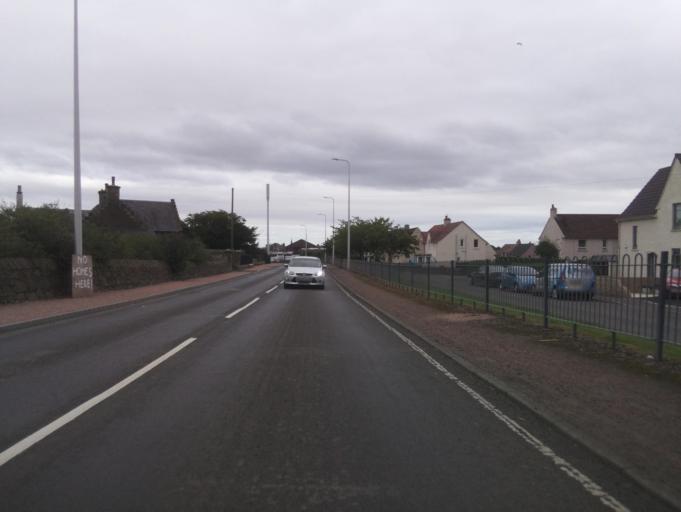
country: GB
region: Scotland
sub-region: Fife
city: Leslie
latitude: 56.2020
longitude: -3.2235
